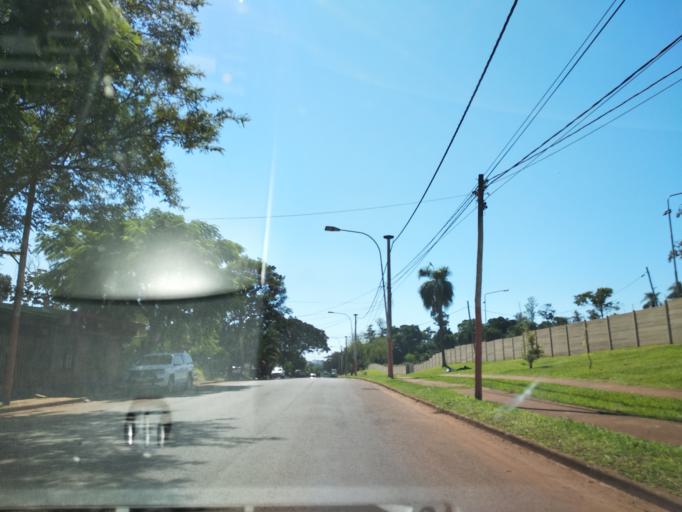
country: AR
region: Misiones
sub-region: Departamento de Iguazu
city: Puerto Iguazu
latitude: -25.6012
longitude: -54.5672
